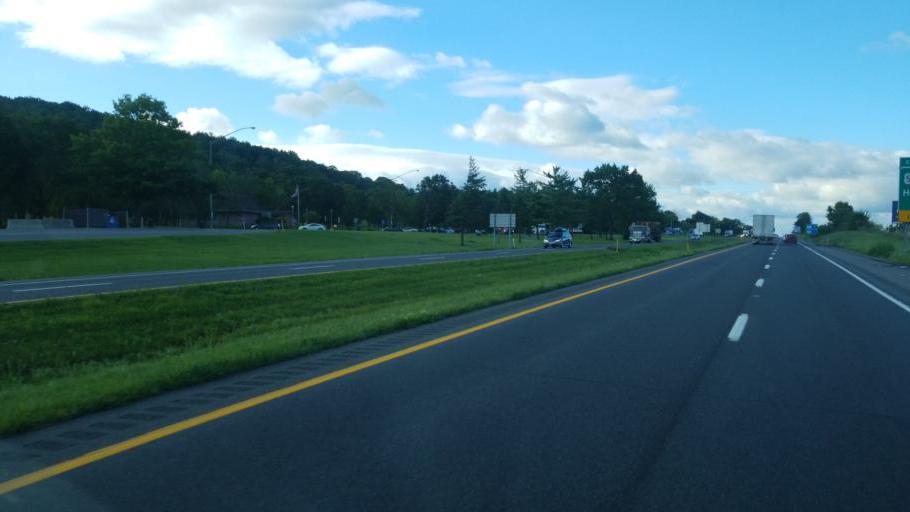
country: US
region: Maryland
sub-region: Washington County
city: Hancock
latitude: 39.7383
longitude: -78.1816
